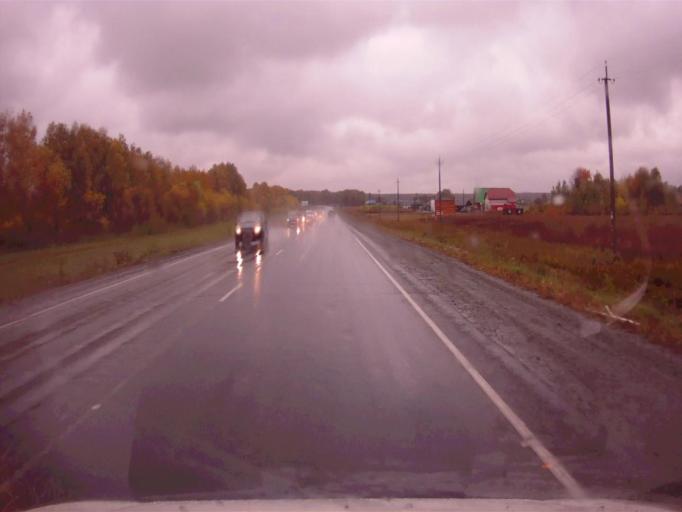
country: RU
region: Chelyabinsk
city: Argayash
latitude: 55.4063
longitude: 61.0587
